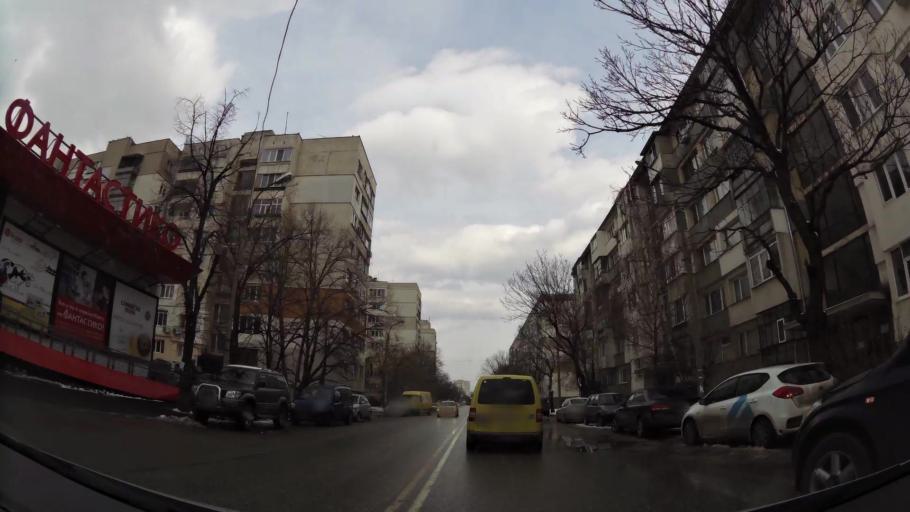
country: BG
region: Sofia-Capital
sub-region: Stolichna Obshtina
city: Sofia
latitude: 42.7046
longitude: 23.3675
